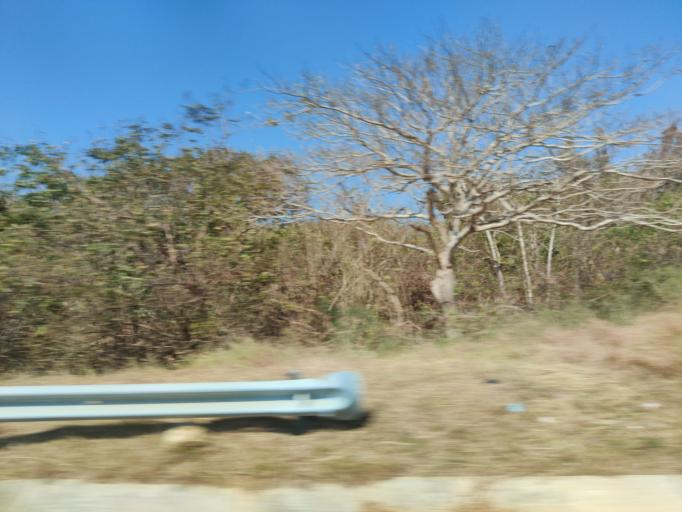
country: CO
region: Atlantico
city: Puerto Colombia
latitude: 10.9544
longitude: -75.0039
